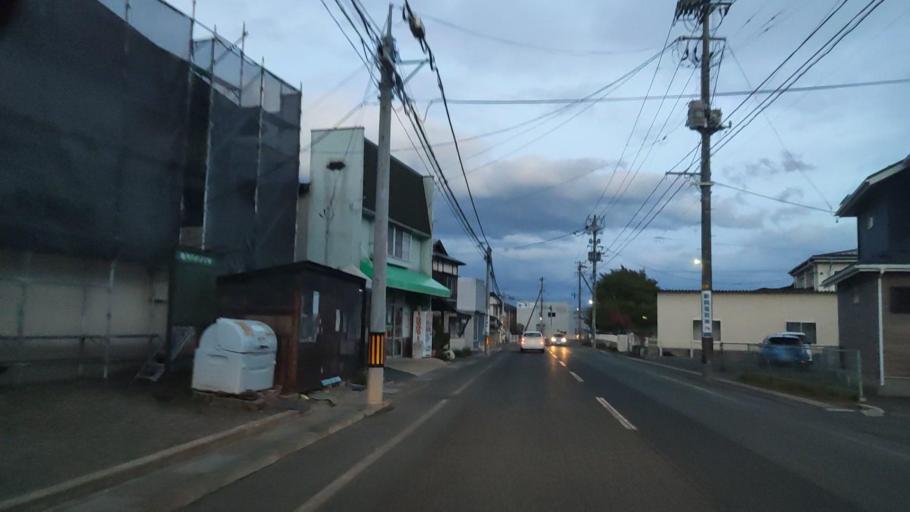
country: JP
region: Iwate
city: Morioka-shi
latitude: 39.7199
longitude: 141.1207
